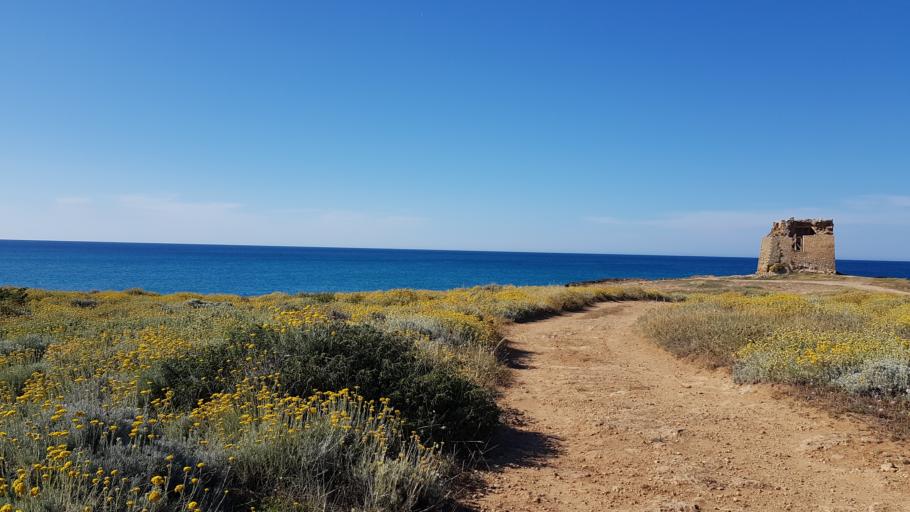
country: IT
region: Apulia
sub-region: Provincia di Brindisi
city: Brindisi
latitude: 40.6873
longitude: 17.8691
